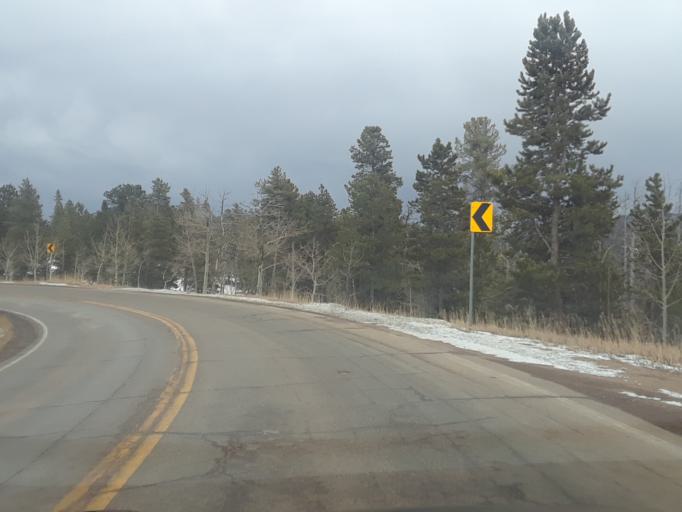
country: US
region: Colorado
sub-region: Gilpin County
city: Central City
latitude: 39.8400
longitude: -105.4674
